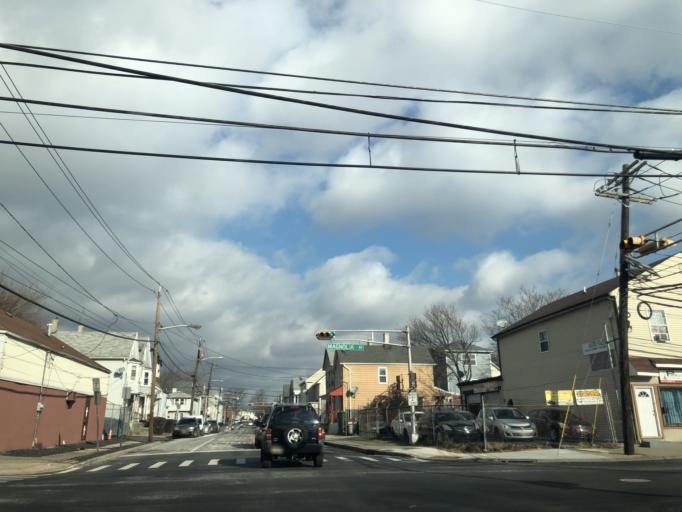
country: US
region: New Jersey
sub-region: Union County
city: Elizabeth
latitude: 40.6674
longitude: -74.2064
